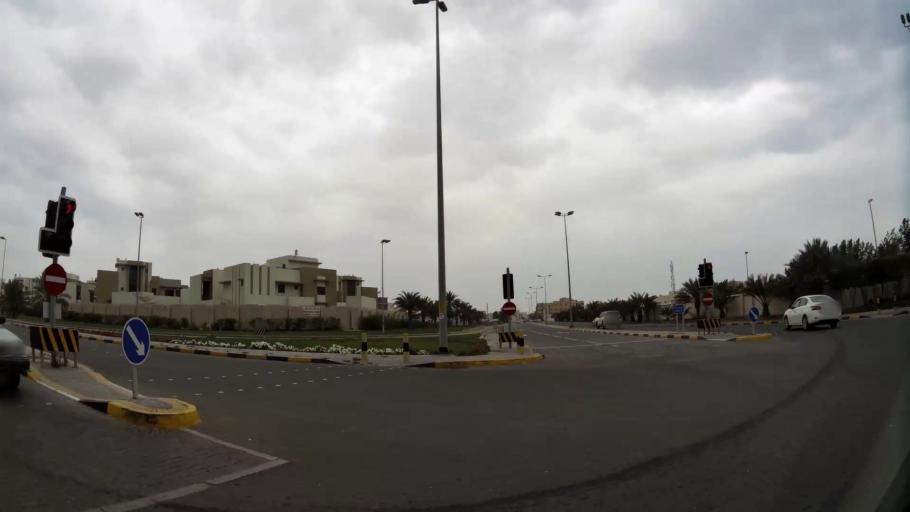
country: BH
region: Central Governorate
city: Dar Kulayb
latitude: 26.0540
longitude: 50.4866
